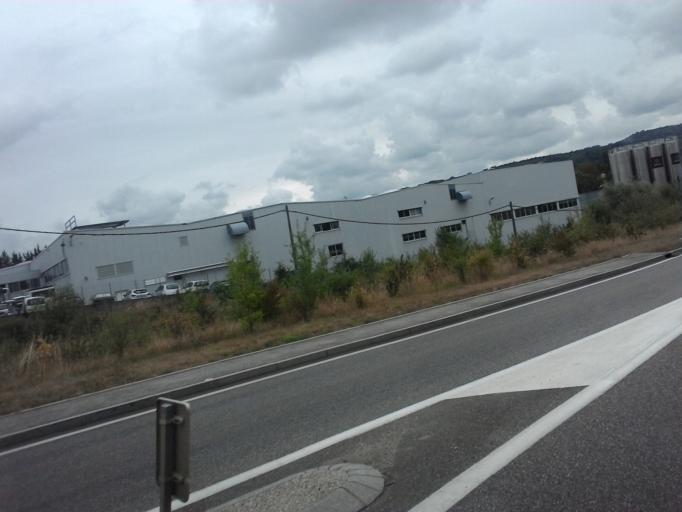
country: FR
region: Franche-Comte
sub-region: Departement du Jura
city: Montmorot
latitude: 46.6607
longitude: 5.5072
